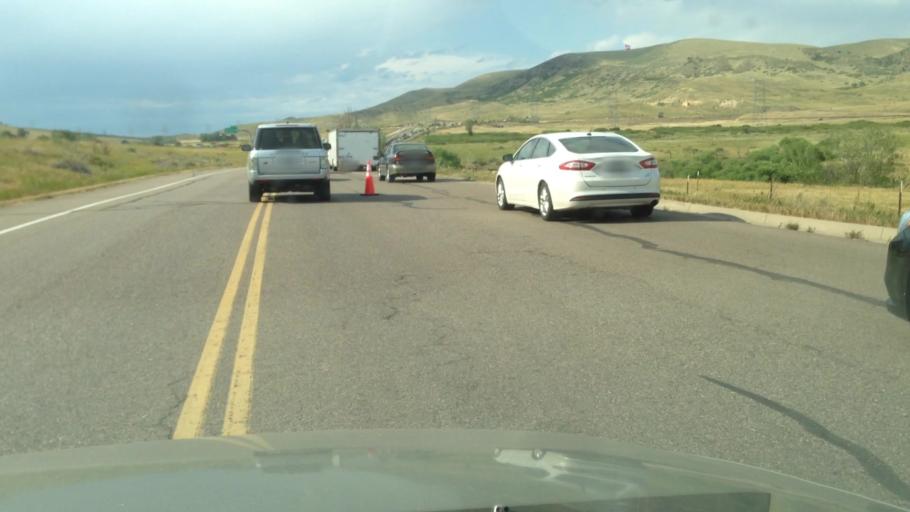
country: US
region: Colorado
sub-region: Jefferson County
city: West Pleasant View
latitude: 39.6757
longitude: -105.1881
